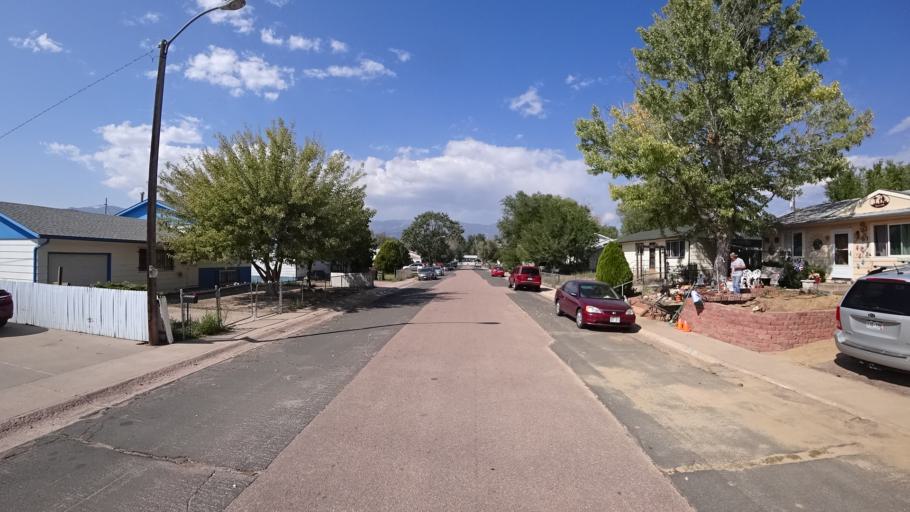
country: US
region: Colorado
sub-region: El Paso County
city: Colorado Springs
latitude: 38.8182
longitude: -104.7875
